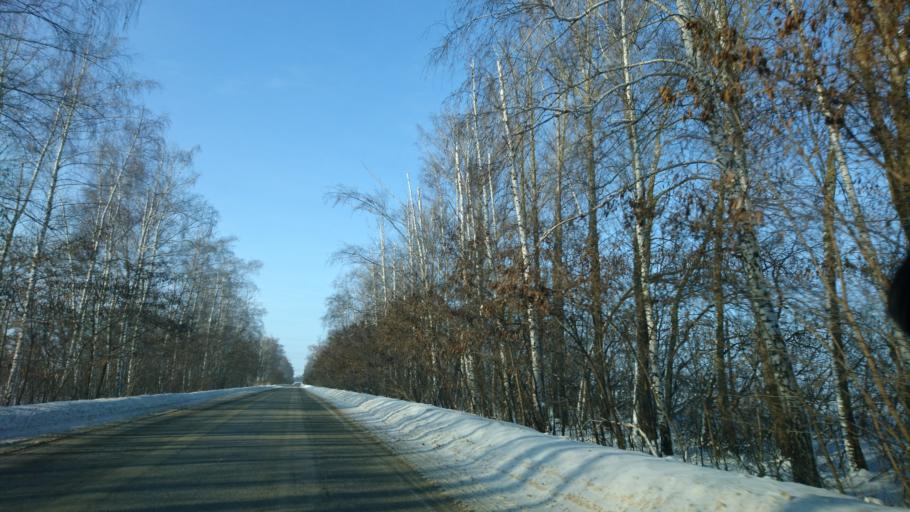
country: RU
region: Belgorod
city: Severnyy
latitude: 50.7285
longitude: 36.5438
